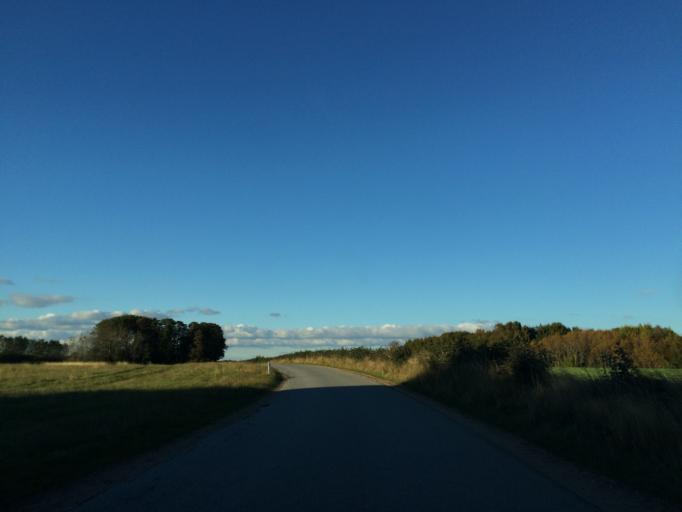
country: DK
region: Central Jutland
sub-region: Silkeborg Kommune
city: Svejbaek
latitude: 56.1764
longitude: 9.6935
